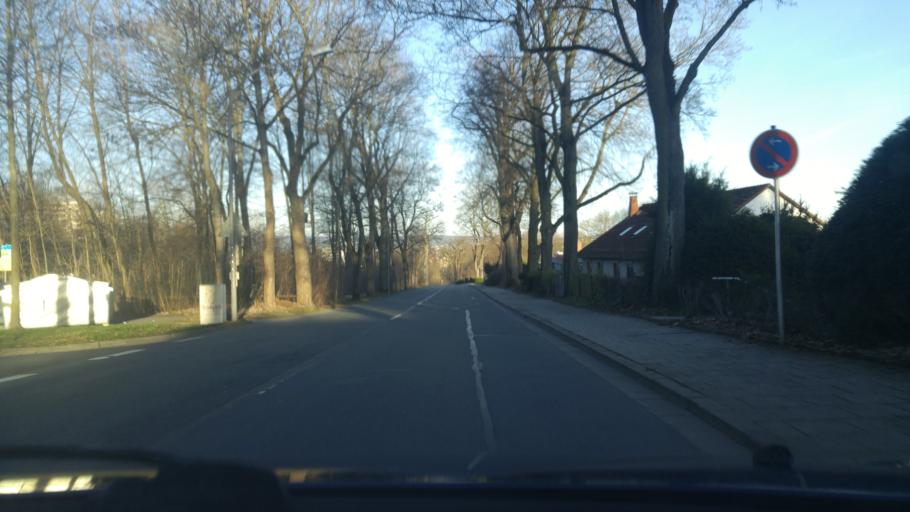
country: DE
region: Bavaria
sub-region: Upper Franconia
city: Heinersreuth
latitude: 49.9362
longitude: 11.5392
